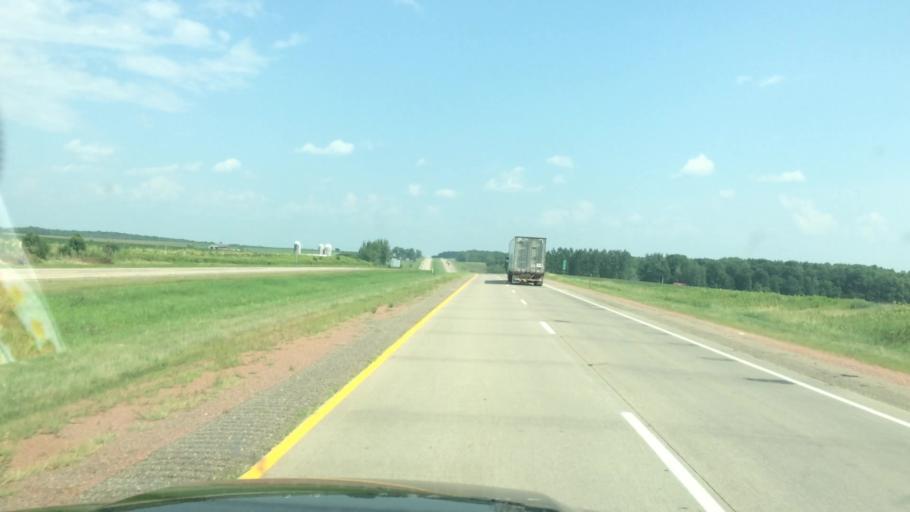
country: US
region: Wisconsin
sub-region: Marathon County
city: Athens
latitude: 44.9442
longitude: -90.0619
